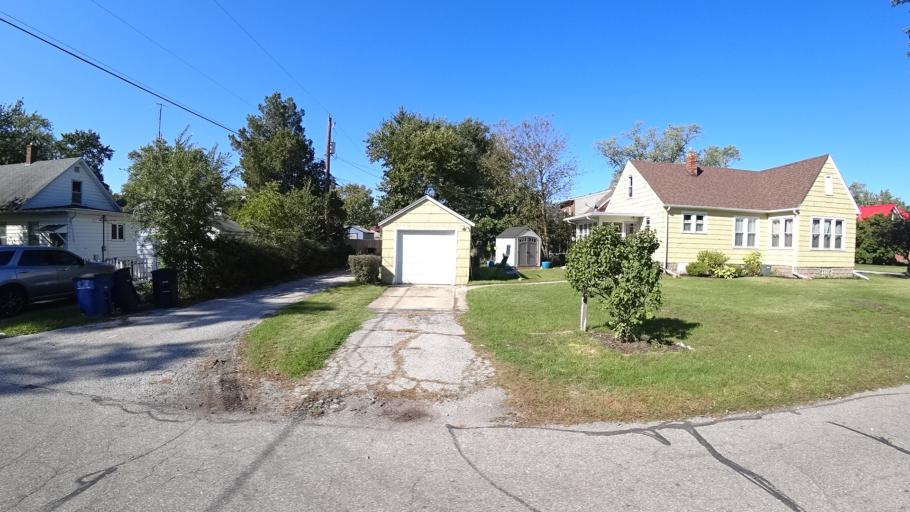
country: US
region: Indiana
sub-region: LaPorte County
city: Michigan City
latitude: 41.7095
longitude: -86.8908
